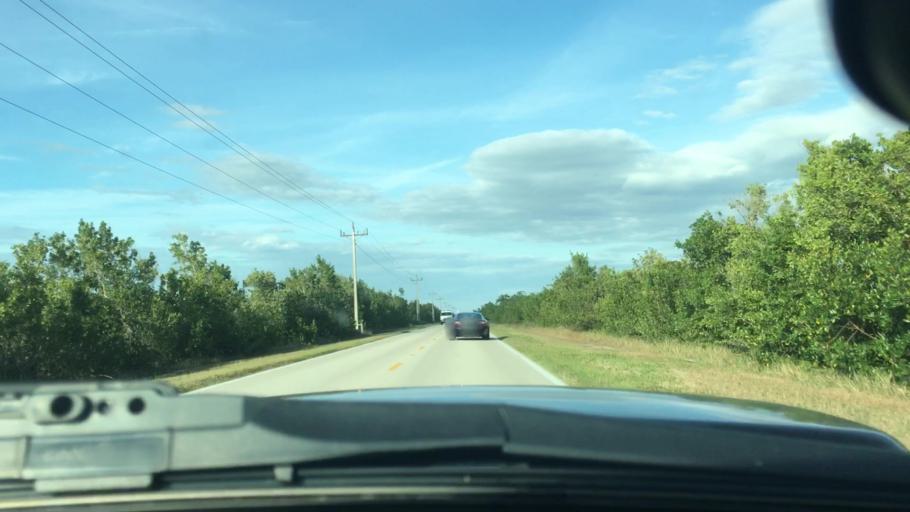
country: US
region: Florida
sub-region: Collier County
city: Marco
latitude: 25.9509
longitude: -81.6415
